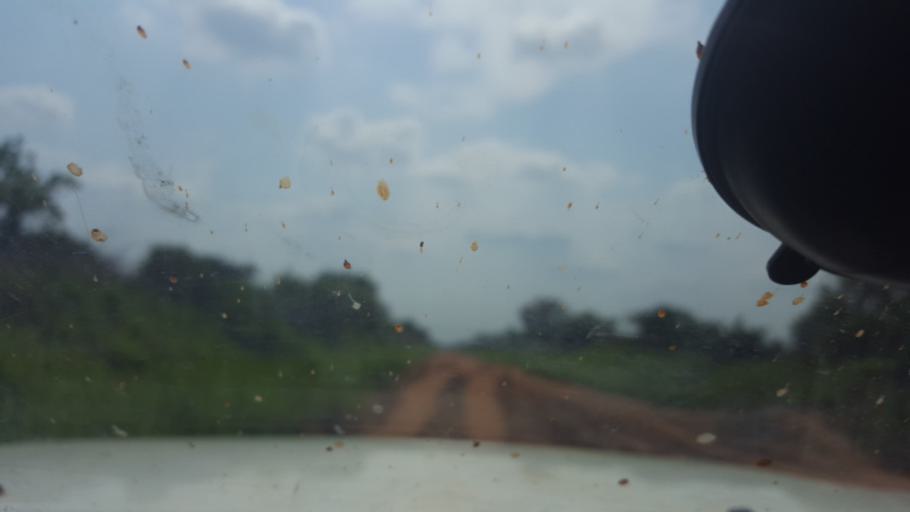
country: CD
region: Bandundu
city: Bandundu
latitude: -3.7618
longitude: 17.1401
